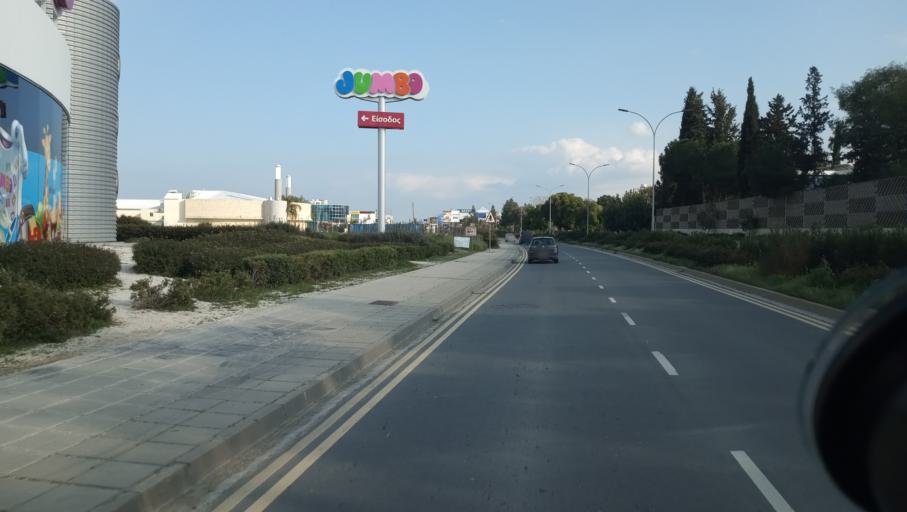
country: CY
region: Lefkosia
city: Tseri
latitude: 35.1286
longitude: 33.3186
